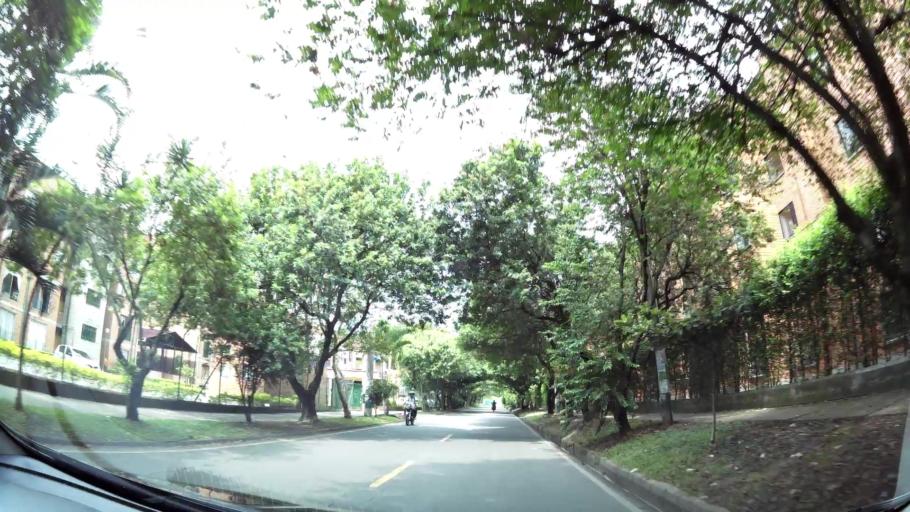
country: CO
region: Antioquia
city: Itagui
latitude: 6.1946
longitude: -75.5925
